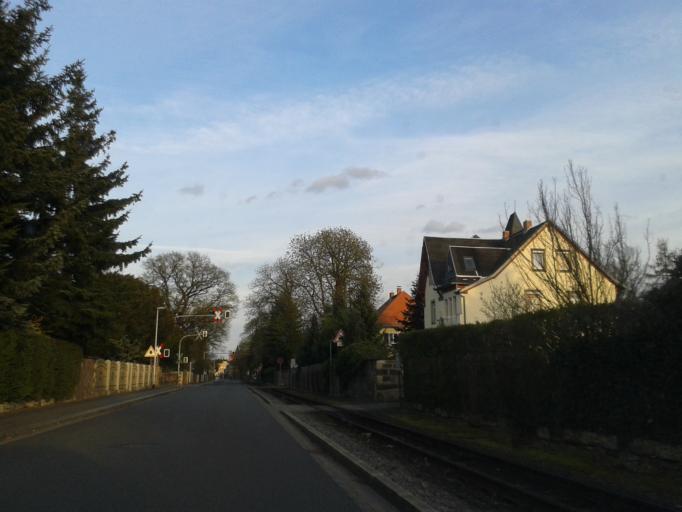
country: DE
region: Saxony
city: Radebeul
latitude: 51.1030
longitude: 13.6655
